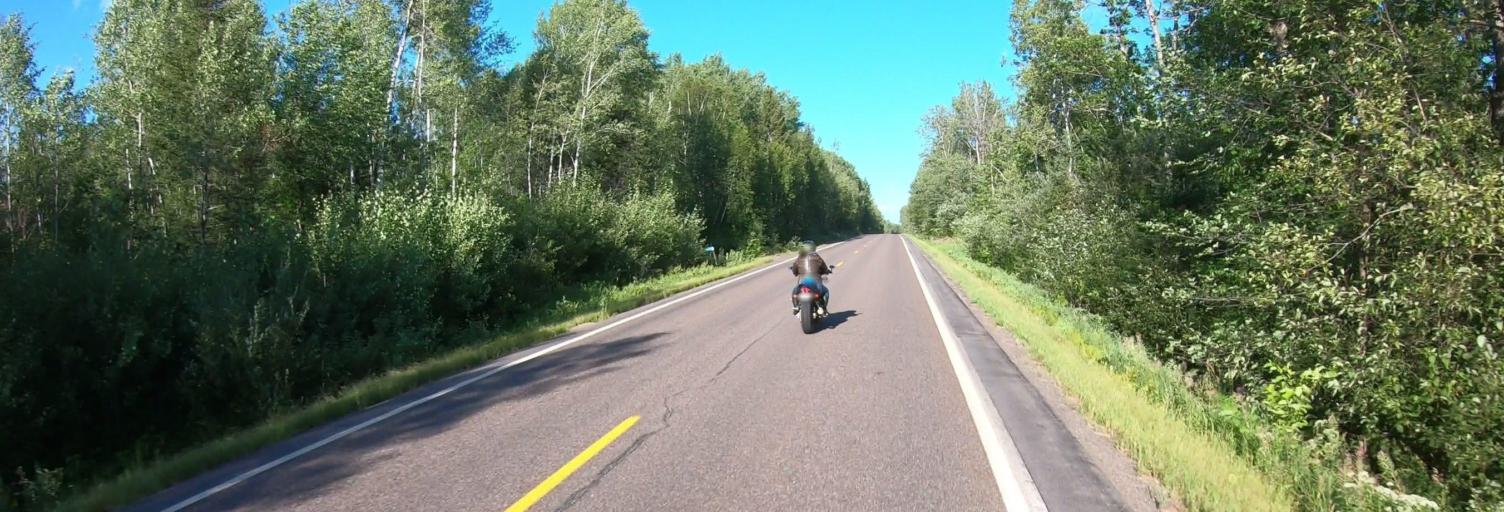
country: US
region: Minnesota
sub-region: Saint Louis County
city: Ely
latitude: 47.9574
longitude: -91.6304
